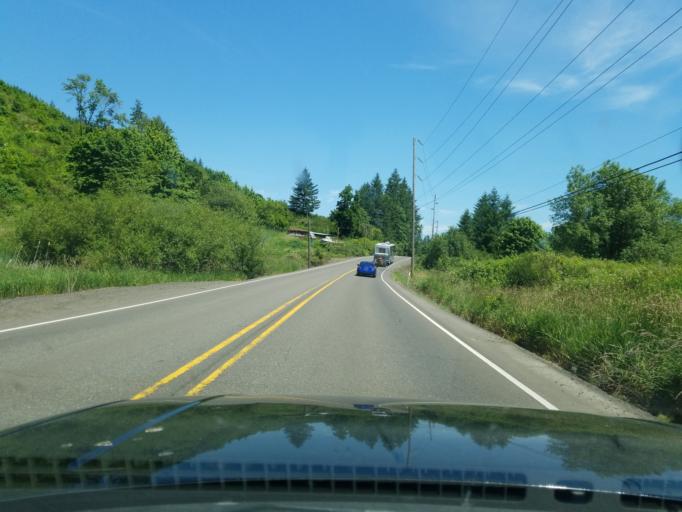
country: US
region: Oregon
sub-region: Yamhill County
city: Yamhill
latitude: 45.3863
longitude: -123.1389
